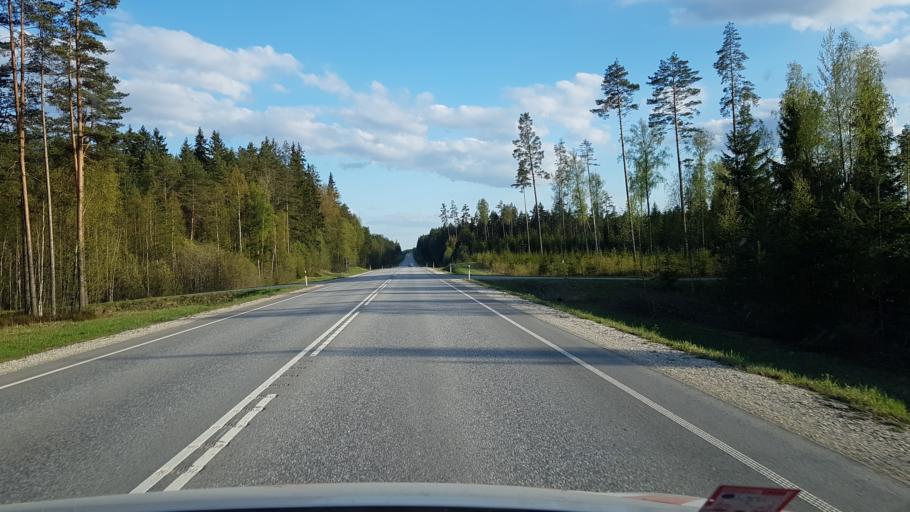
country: EE
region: Vorumaa
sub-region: Voru linn
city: Voru
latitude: 57.9491
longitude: 26.7947
